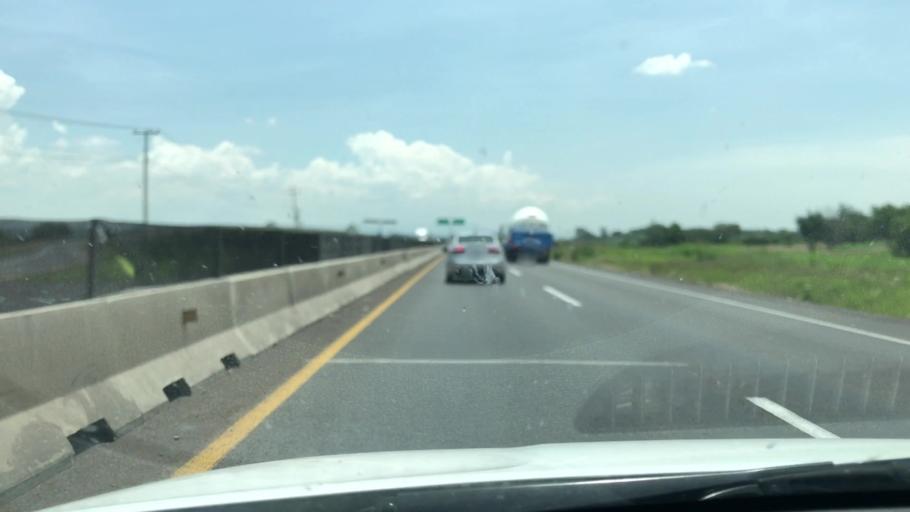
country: MX
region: Jalisco
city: Degollado
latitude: 20.3661
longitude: -102.1324
